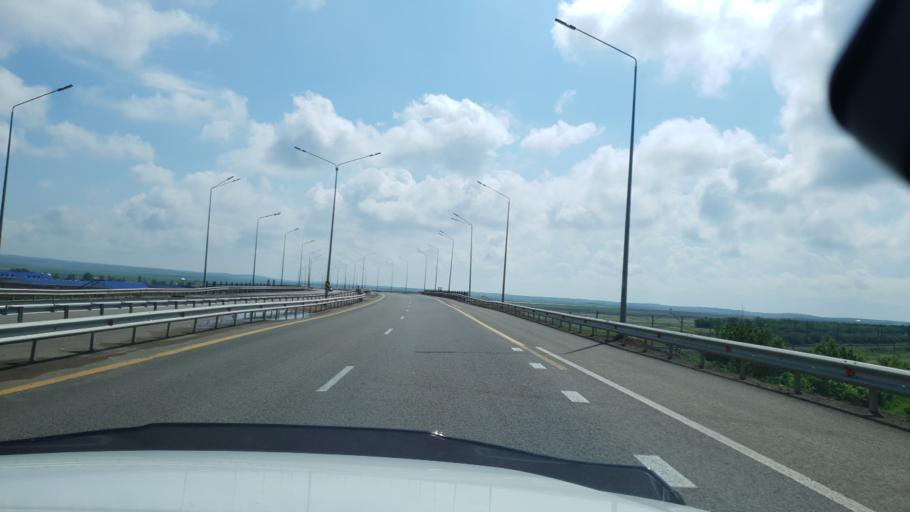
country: KZ
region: Qaraghandy
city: Osakarovka
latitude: 50.8111
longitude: 72.1755
